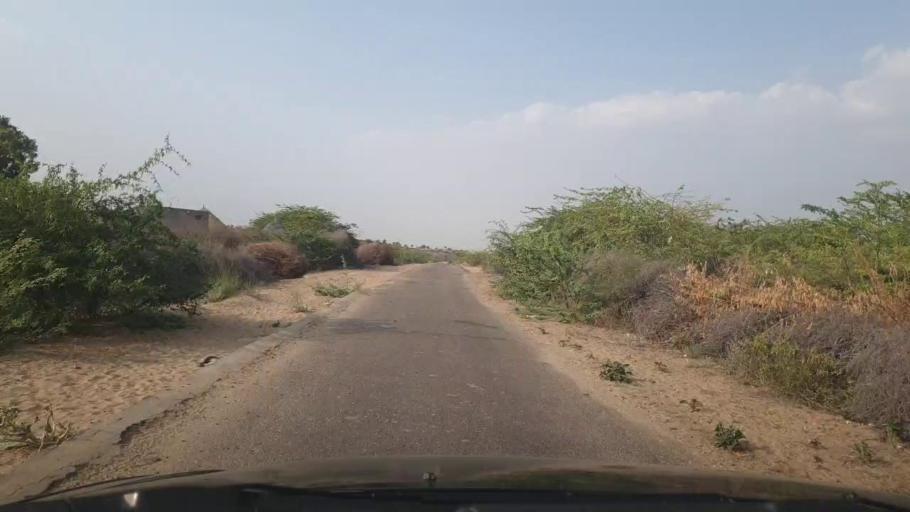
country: PK
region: Sindh
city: Islamkot
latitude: 25.0685
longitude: 70.5656
